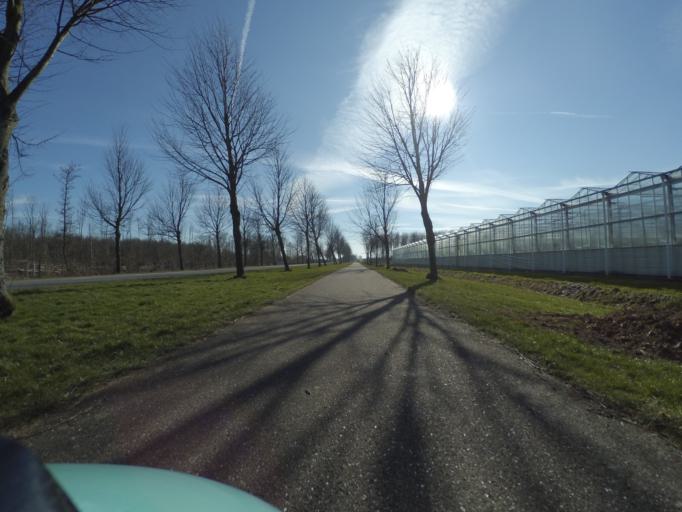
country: NL
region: Flevoland
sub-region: Gemeente Almere
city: Almere Stad
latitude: 52.4245
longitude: 5.2649
